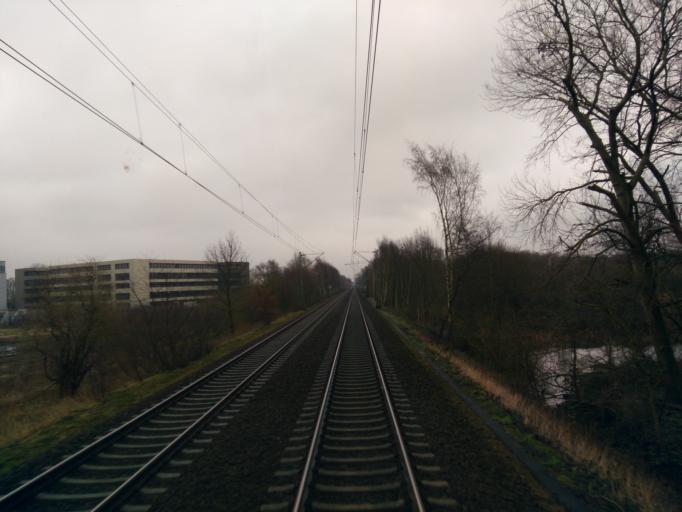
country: DE
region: Bremen
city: Bremen
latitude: 53.1002
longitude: 8.8519
